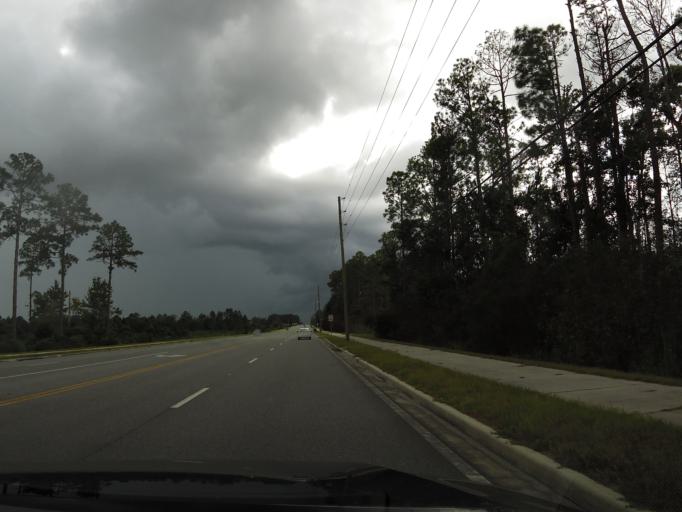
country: US
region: Florida
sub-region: Clay County
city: Asbury Lake
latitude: 30.0628
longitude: -81.8094
